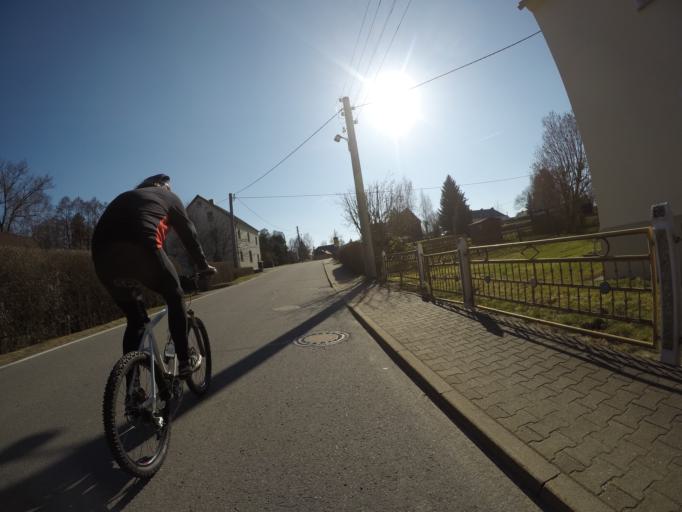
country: DE
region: Saxony
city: Grosshartmannsdorf
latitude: 50.8290
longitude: 13.3622
